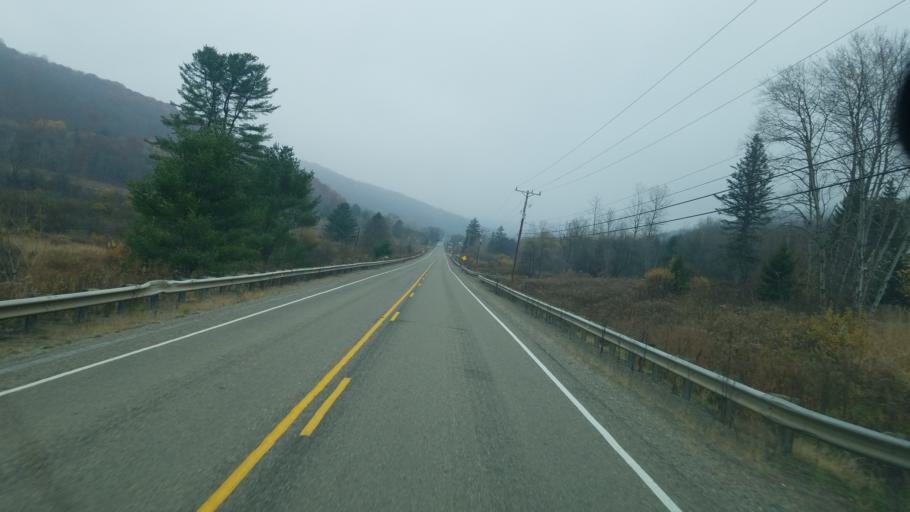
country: US
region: Pennsylvania
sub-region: McKean County
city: Smethport
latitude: 41.8808
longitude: -78.4914
